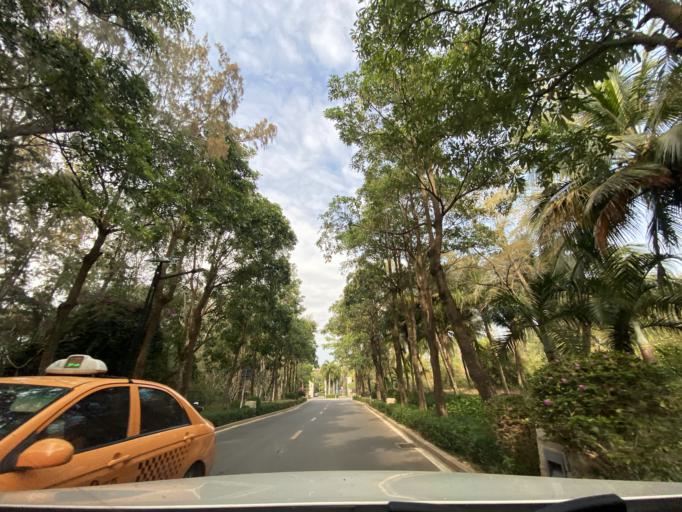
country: CN
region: Hainan
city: Tiandu
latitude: 18.2219
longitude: 109.6182
